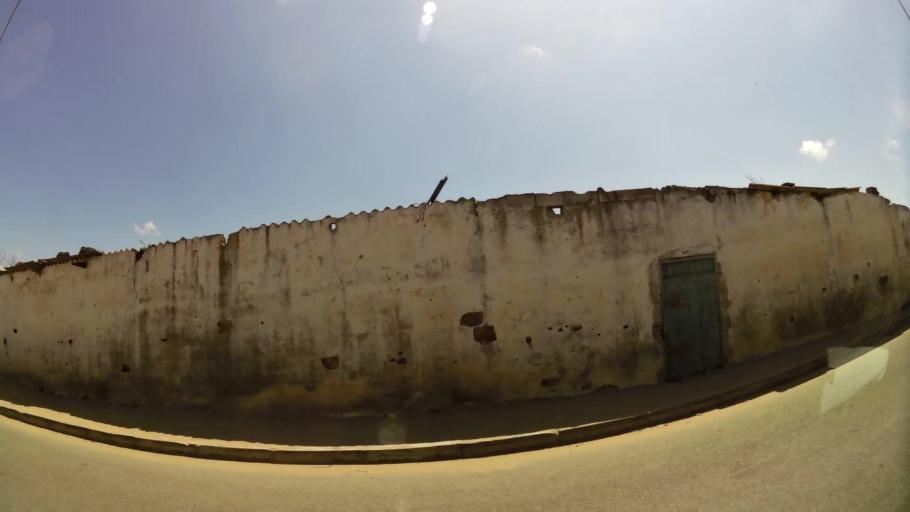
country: MA
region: Gharb-Chrarda-Beni Hssen
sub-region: Kenitra Province
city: Kenitra
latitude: 34.2297
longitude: -6.5361
